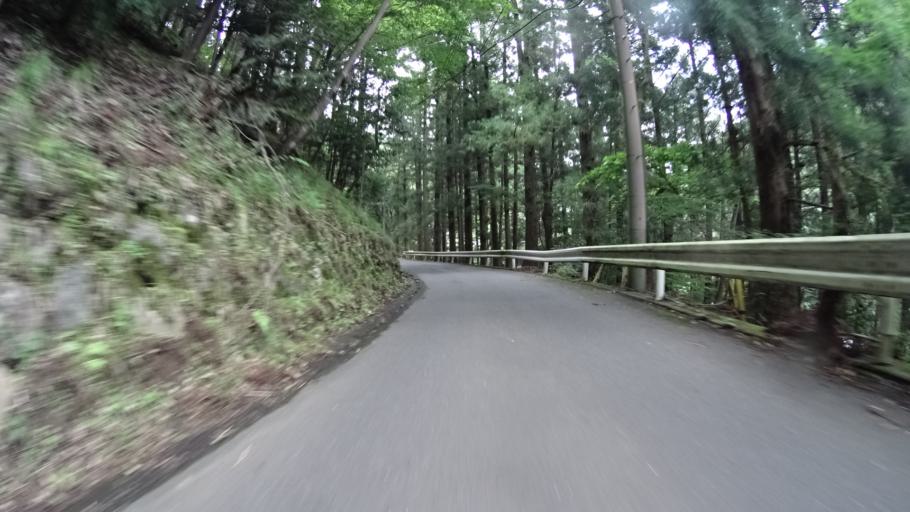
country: JP
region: Kanagawa
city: Hadano
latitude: 35.4919
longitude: 139.2198
